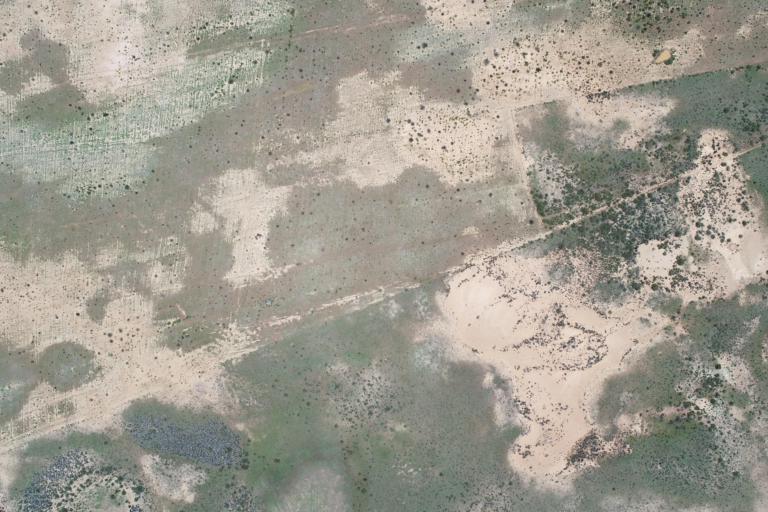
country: BO
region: La Paz
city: Patacamaya
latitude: -17.2840
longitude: -68.5039
